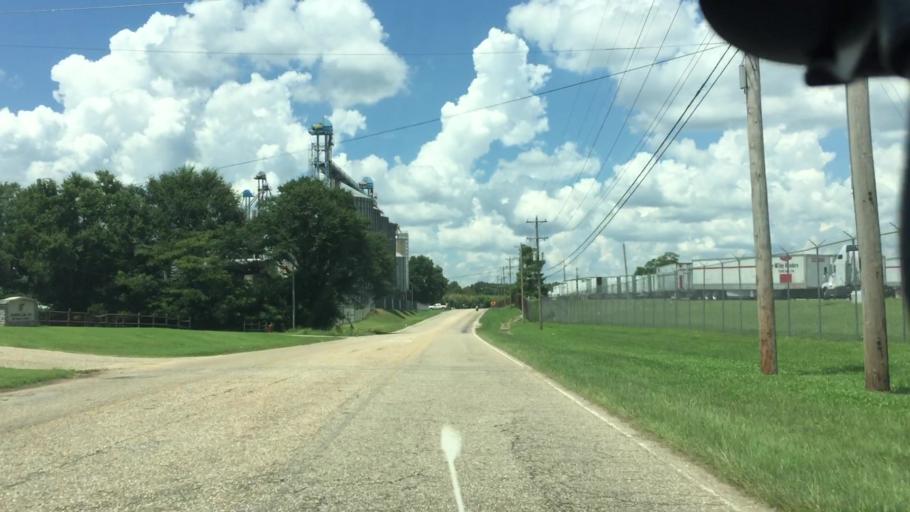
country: US
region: Alabama
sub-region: Pike County
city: Troy
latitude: 31.7822
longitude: -85.9801
